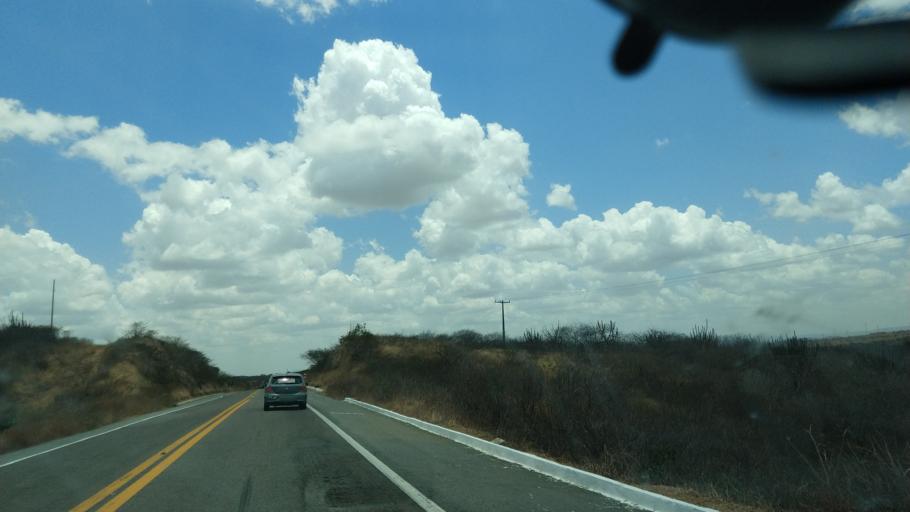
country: BR
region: Rio Grande do Norte
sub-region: Cerro Cora
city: Cerro Cora
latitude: -6.1994
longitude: -36.2704
